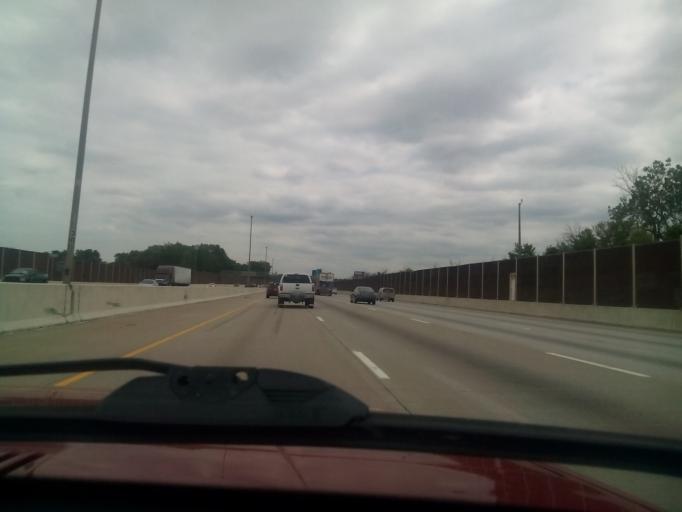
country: US
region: Indiana
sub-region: Lake County
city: Highland
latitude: 41.5740
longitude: -87.4549
